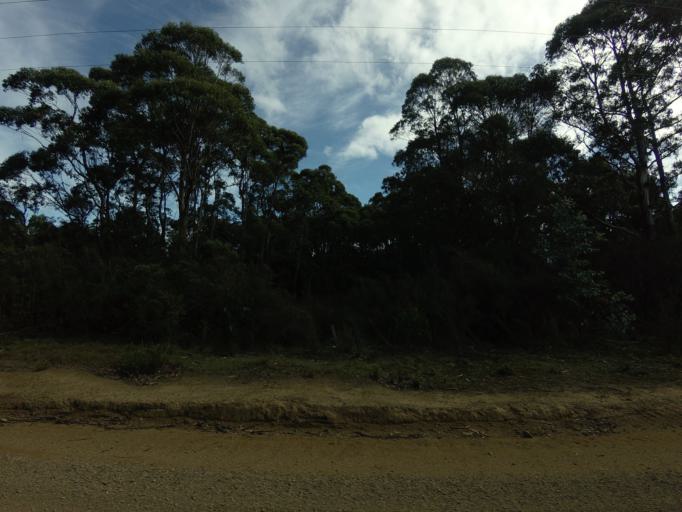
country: AU
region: Tasmania
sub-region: Clarence
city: Sandford
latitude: -43.1626
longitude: 147.7683
